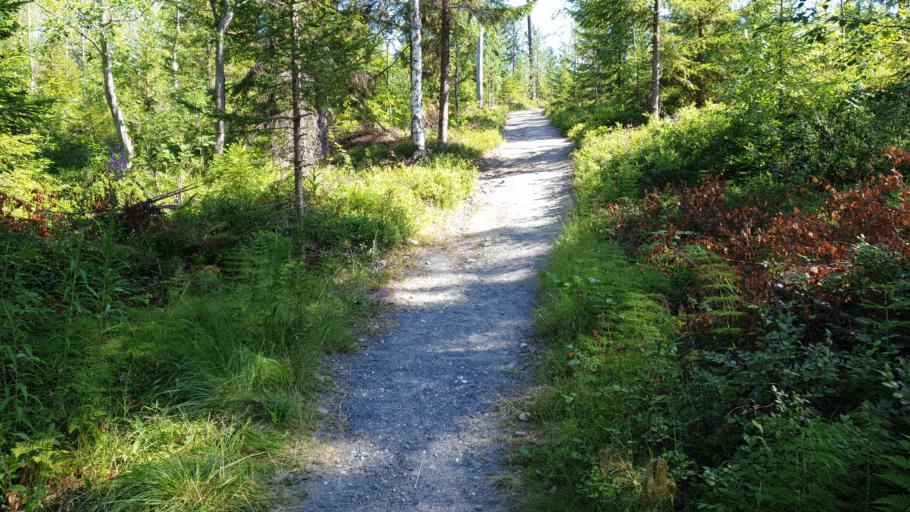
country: SE
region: Vaesternorrland
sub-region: OErnskoeldsviks Kommun
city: Husum
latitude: 63.4963
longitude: 18.9279
